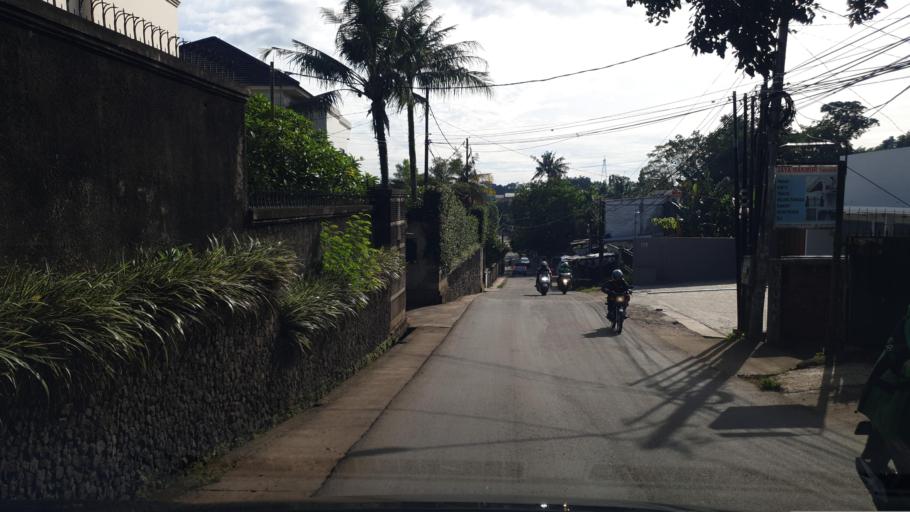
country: ID
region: West Java
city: Sawangan
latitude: -6.3604
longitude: 106.7776
